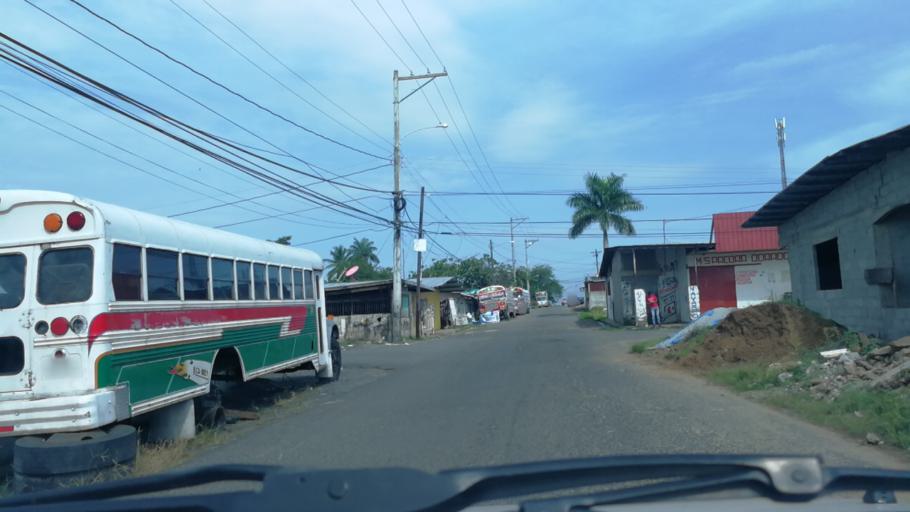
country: PA
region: Panama
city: Pacora
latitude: 9.0838
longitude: -79.2913
